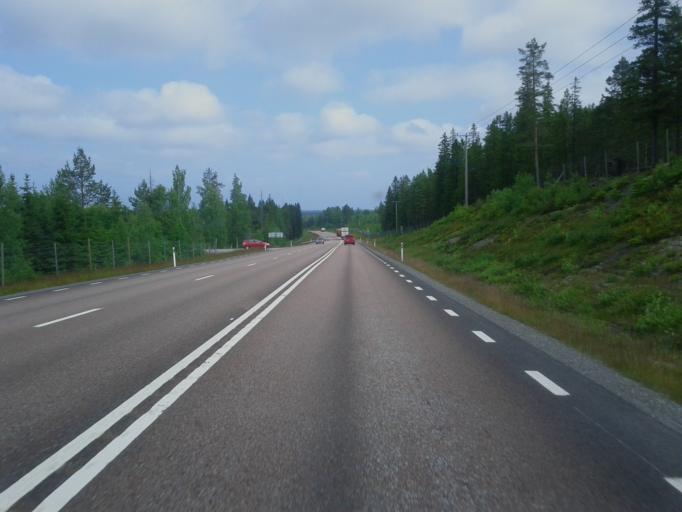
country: SE
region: Vaesterbotten
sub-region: Skelleftea Kommun
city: Burea
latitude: 64.4566
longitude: 21.2876
